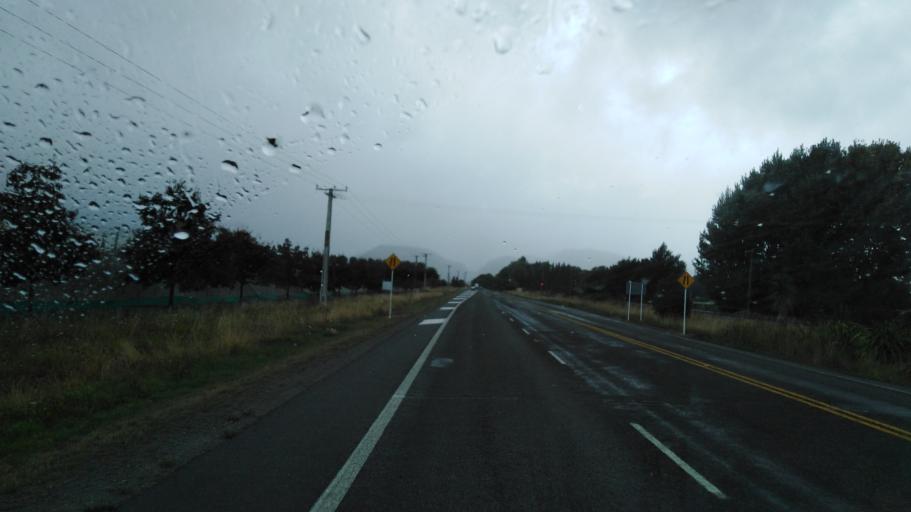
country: NZ
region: Marlborough
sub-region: Marlborough District
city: Blenheim
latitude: -41.4525
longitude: 173.9626
